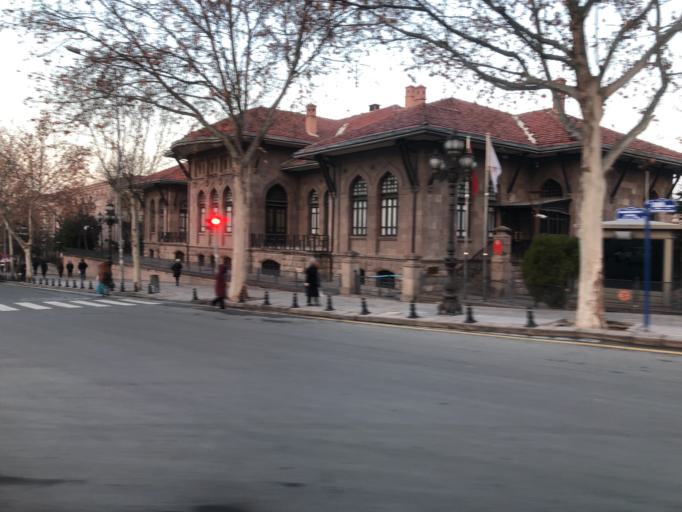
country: TR
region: Ankara
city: Ankara
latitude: 39.9421
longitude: 32.8541
